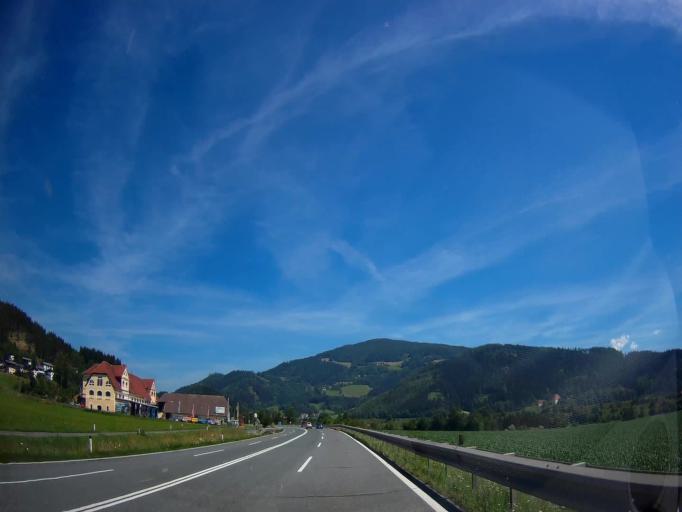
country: AT
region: Carinthia
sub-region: Politischer Bezirk Sankt Veit an der Glan
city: Althofen
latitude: 46.8737
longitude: 14.4506
